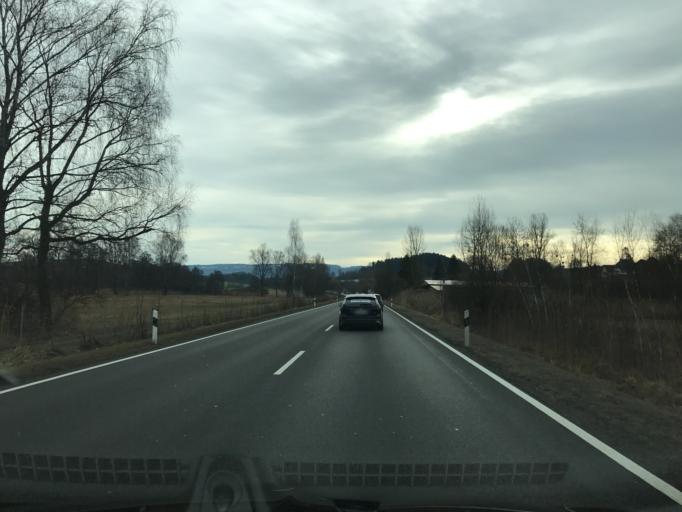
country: DE
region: Bavaria
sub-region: Swabia
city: Bodolz
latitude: 47.5850
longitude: 9.6590
